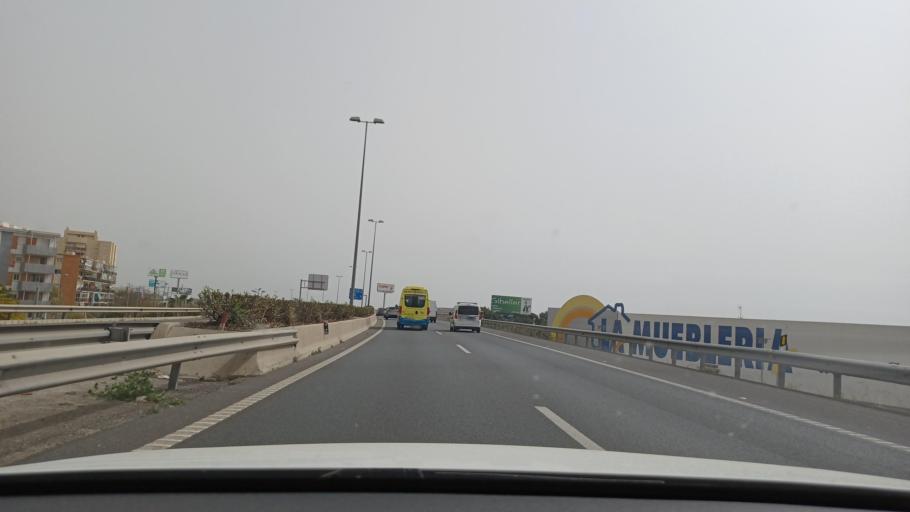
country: ES
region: Valencia
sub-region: Provincia de Alicante
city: San Vicent del Raspeig
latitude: 38.3797
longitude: -0.5034
